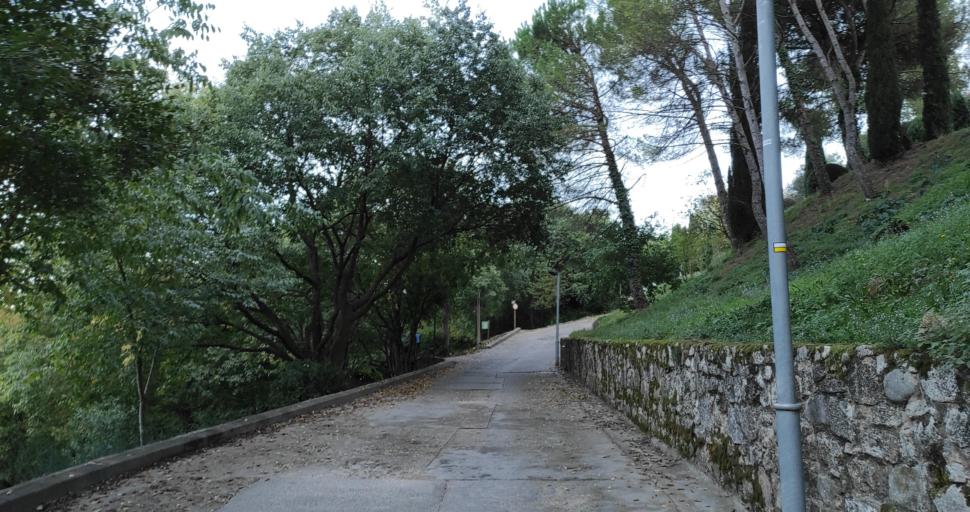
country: ES
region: Catalonia
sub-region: Provincia de Girona
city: Girona
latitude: 41.9872
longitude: 2.8285
